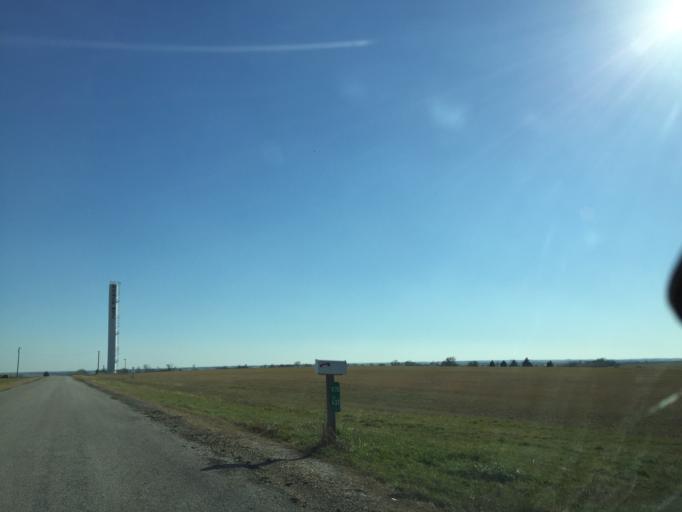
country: US
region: Texas
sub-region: Williamson County
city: Taylor
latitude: 30.5717
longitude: -97.3104
